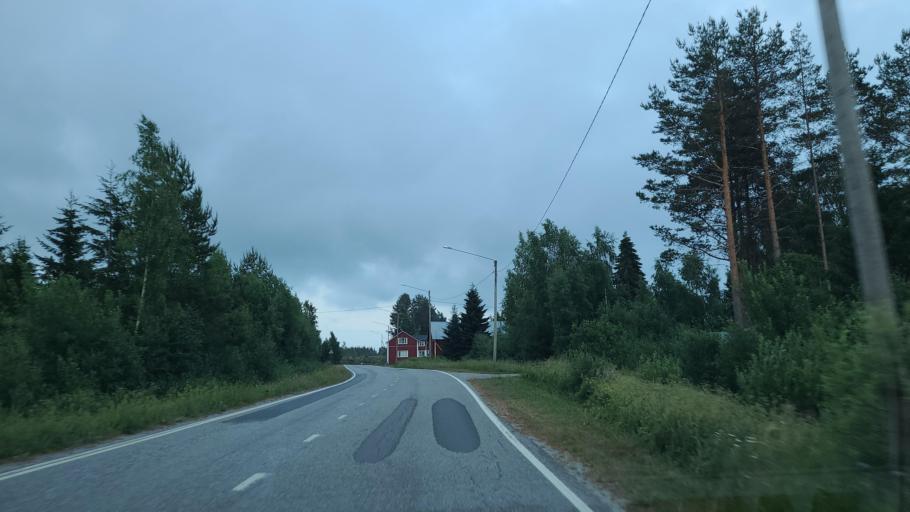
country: FI
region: Ostrobothnia
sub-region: Vaasa
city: Replot
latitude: 63.2844
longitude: 21.1231
